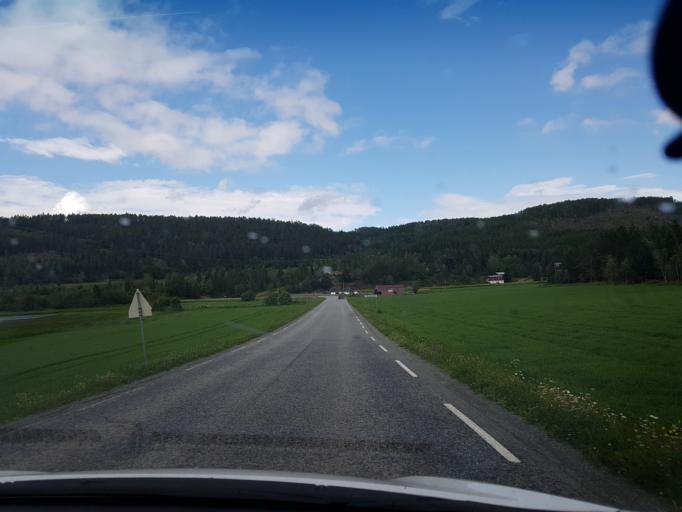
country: NO
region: Nord-Trondelag
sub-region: Stjordal
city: Stjordalshalsen
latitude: 63.6107
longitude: 10.9361
